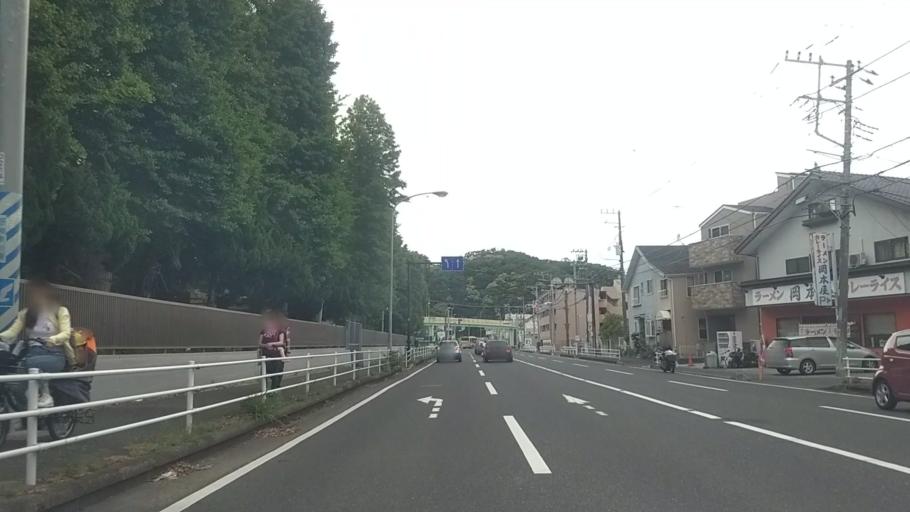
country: JP
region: Kanagawa
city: Kamakura
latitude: 35.3481
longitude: 139.5220
